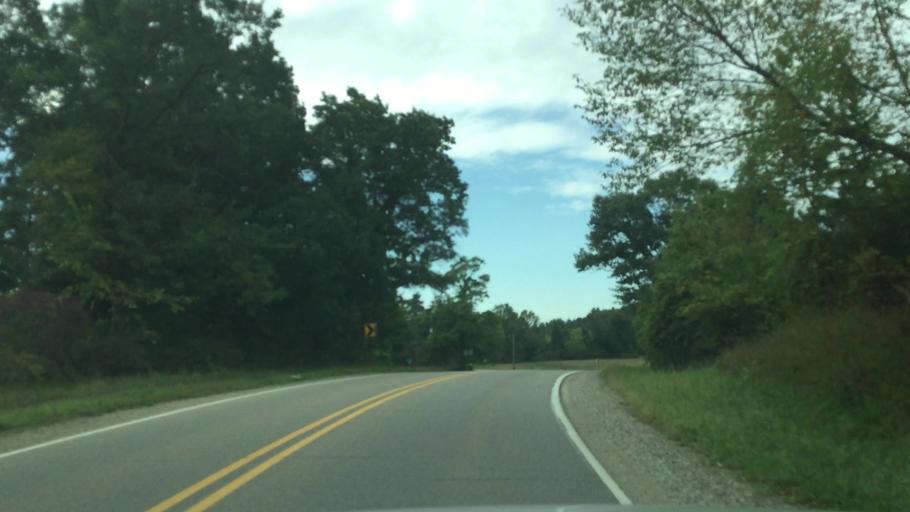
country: US
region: Michigan
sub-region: Genesee County
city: Argentine
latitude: 42.6915
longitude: -83.8382
